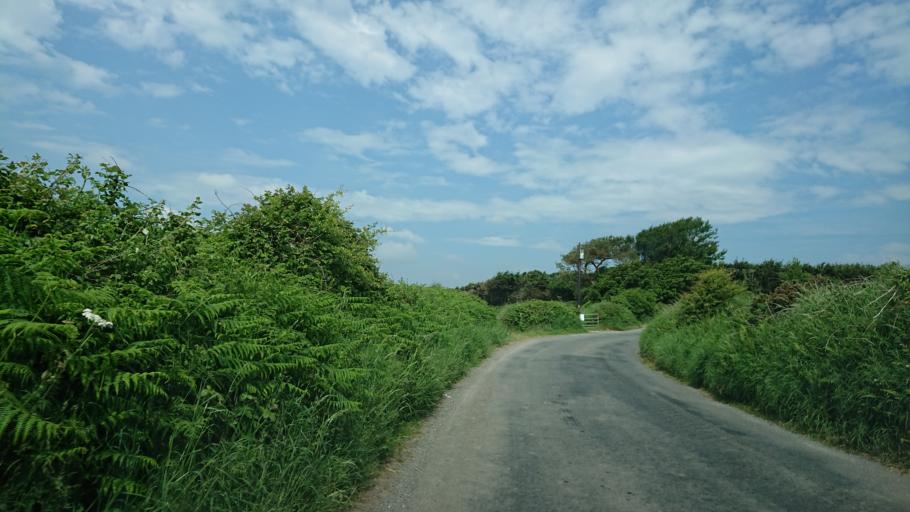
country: IE
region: Munster
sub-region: Waterford
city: Dunmore East
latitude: 52.2285
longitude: -7.0046
